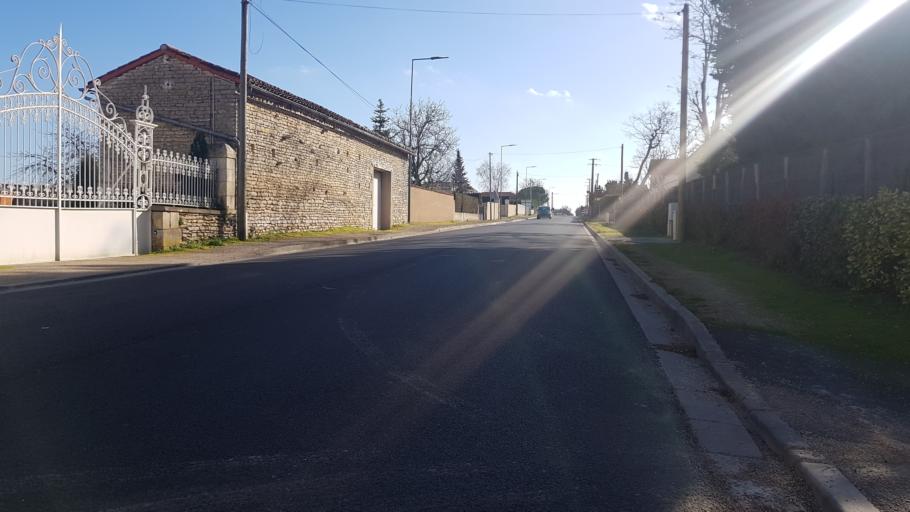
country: FR
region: Poitou-Charentes
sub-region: Departement de la Vienne
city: Avanton
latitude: 46.6598
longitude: 0.3051
